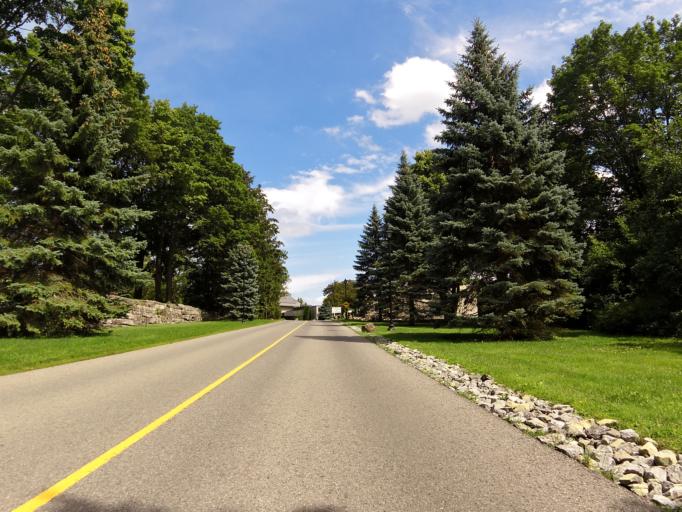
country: CA
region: Ontario
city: Ottawa
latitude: 45.4451
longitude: -75.6682
